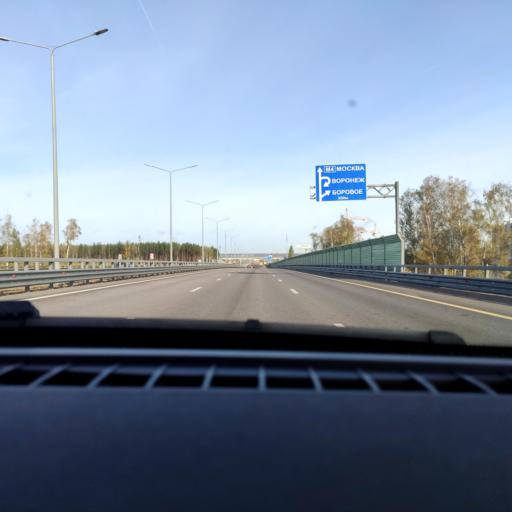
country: RU
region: Voronezj
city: Somovo
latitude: 51.7365
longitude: 39.3094
